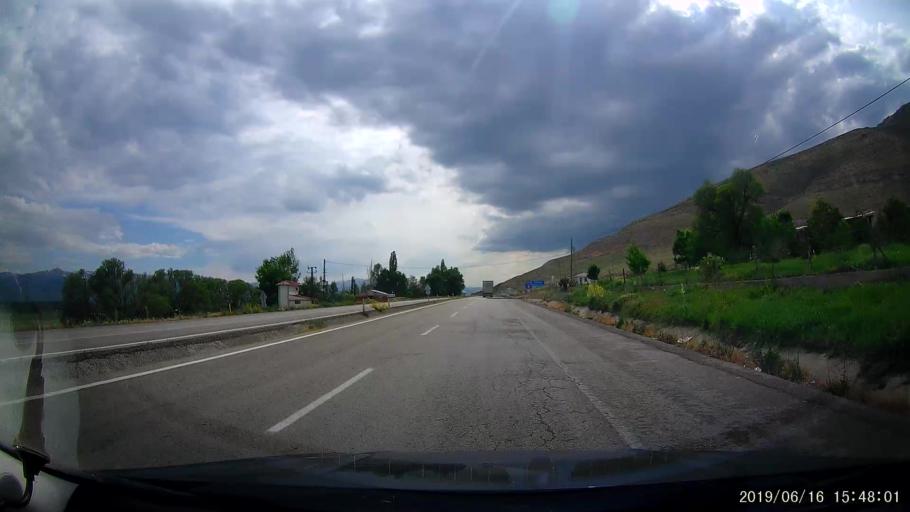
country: TR
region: Erzurum
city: Pasinler
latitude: 39.9860
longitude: 41.7093
